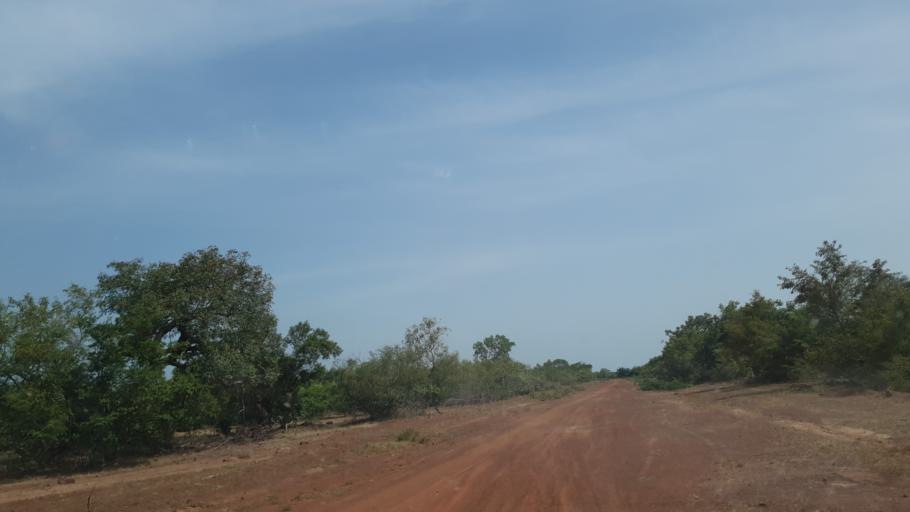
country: ML
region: Koulikoro
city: Dioila
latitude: 12.4469
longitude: -6.2020
